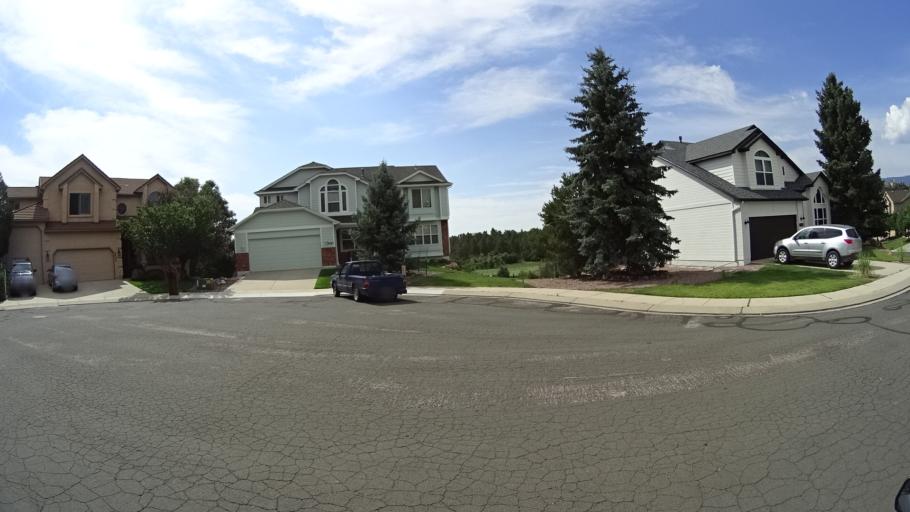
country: US
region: Colorado
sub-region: El Paso County
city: Air Force Academy
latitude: 38.9526
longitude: -104.8599
